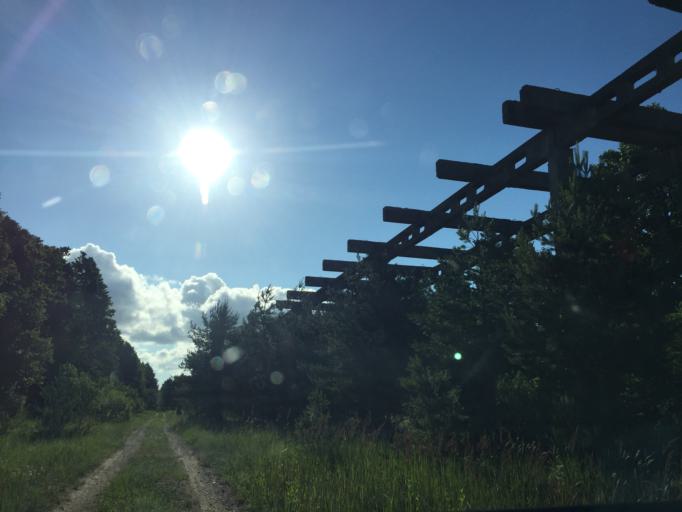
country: LV
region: Ventspils
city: Ventspils
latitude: 57.4103
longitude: 21.6423
